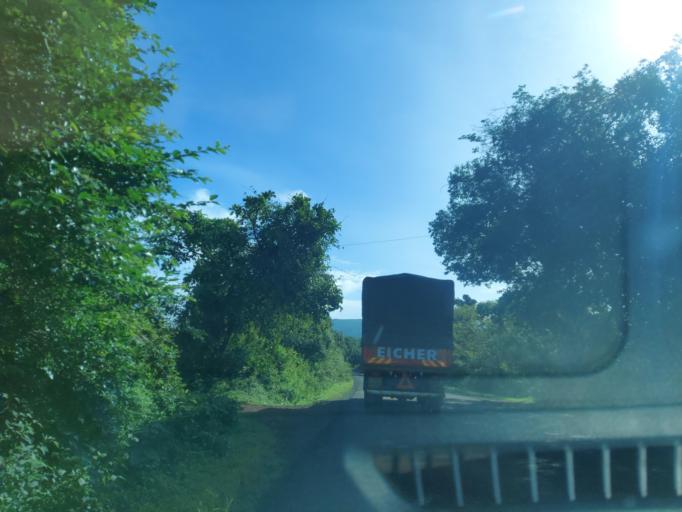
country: IN
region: Maharashtra
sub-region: Kolhapur
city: Ajra
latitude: 16.0076
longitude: 74.0459
